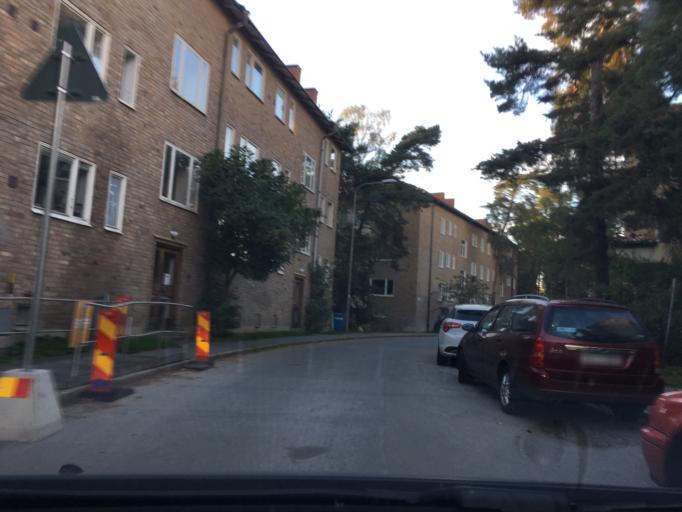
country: SE
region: Stockholm
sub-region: Stockholms Kommun
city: Bromma
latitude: 59.3318
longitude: 17.9523
